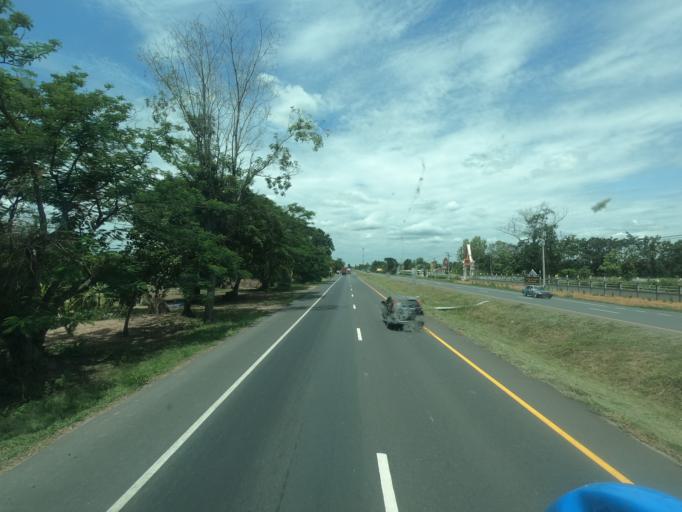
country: TH
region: Buriram
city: Prakhon Chai
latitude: 14.6292
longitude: 103.1960
